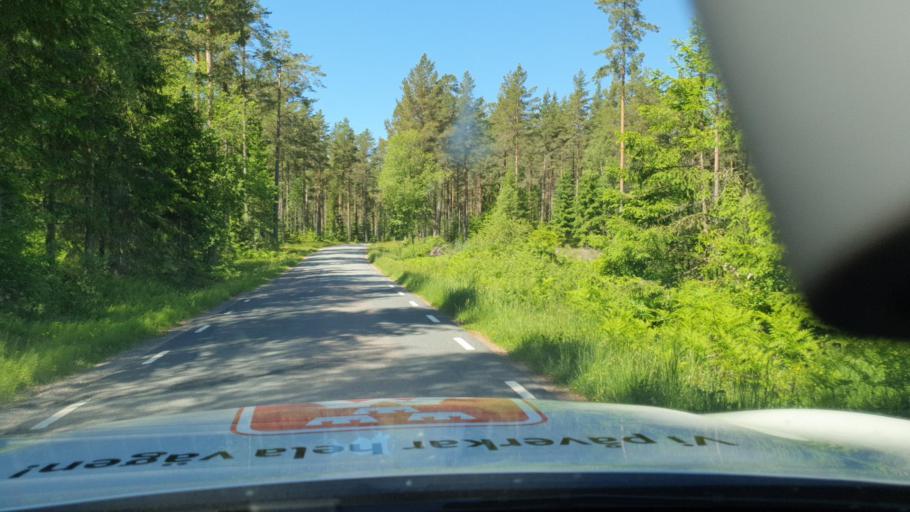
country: SE
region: Joenkoeping
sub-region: Habo Kommun
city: Habo
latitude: 57.8886
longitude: 14.0029
